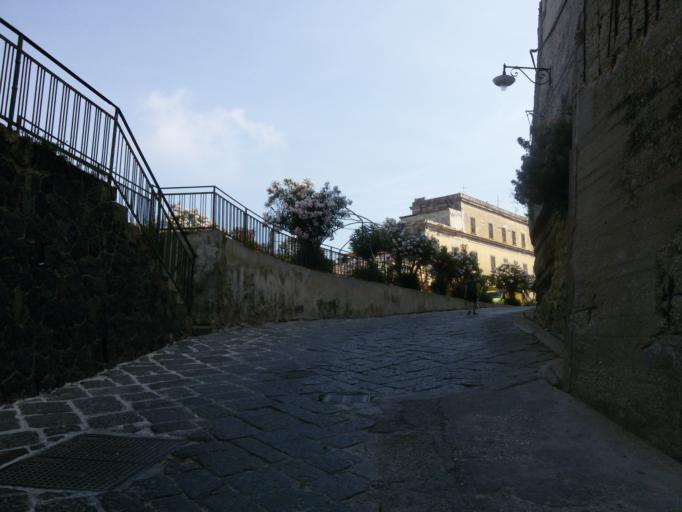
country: IT
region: Campania
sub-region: Provincia di Napoli
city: Procida
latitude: 40.7609
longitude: 14.0334
